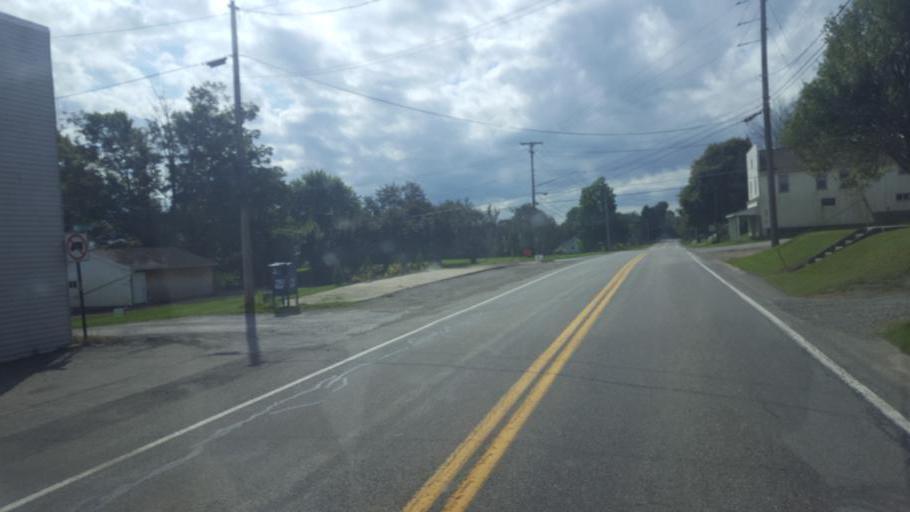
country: US
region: Pennsylvania
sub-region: Mercer County
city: Greenville
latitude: 41.5119
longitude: -80.3698
